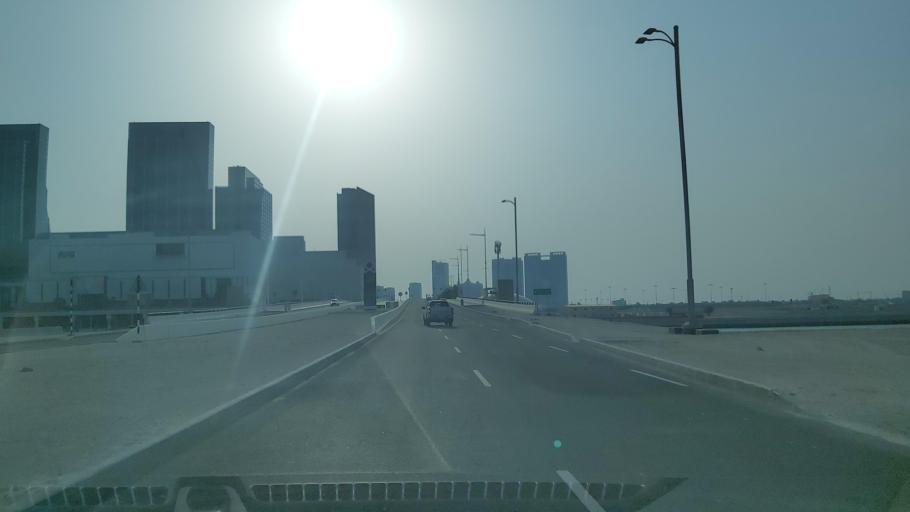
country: AE
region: Abu Dhabi
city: Abu Dhabi
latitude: 24.5029
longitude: 54.3957
